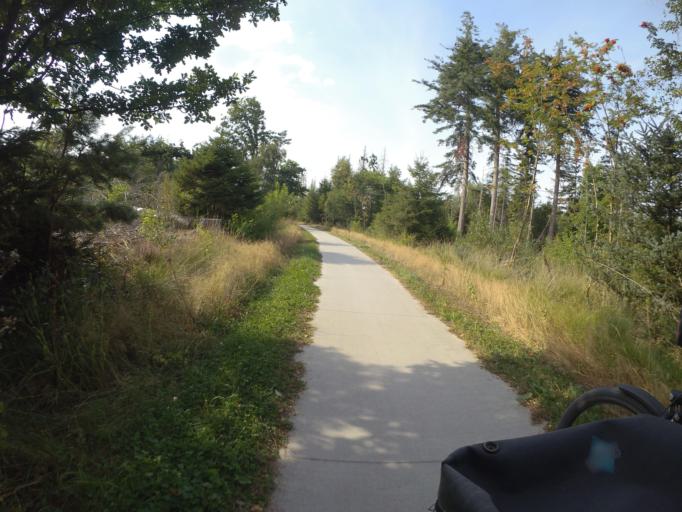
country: NL
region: Drenthe
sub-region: Gemeente Westerveld
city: Dwingeloo
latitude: 52.9096
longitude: 6.3558
